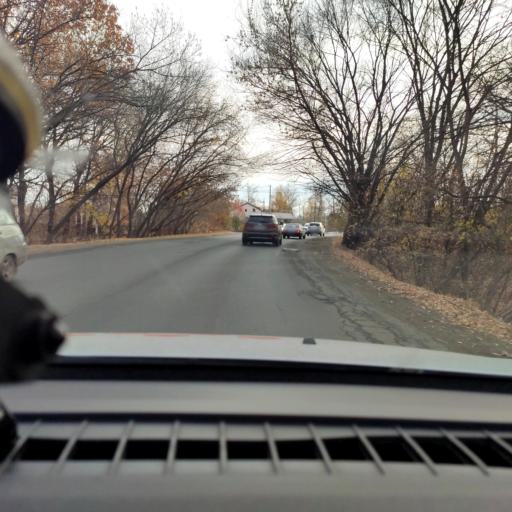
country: RU
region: Samara
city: Novokuybyshevsk
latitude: 53.1454
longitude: 50.0139
